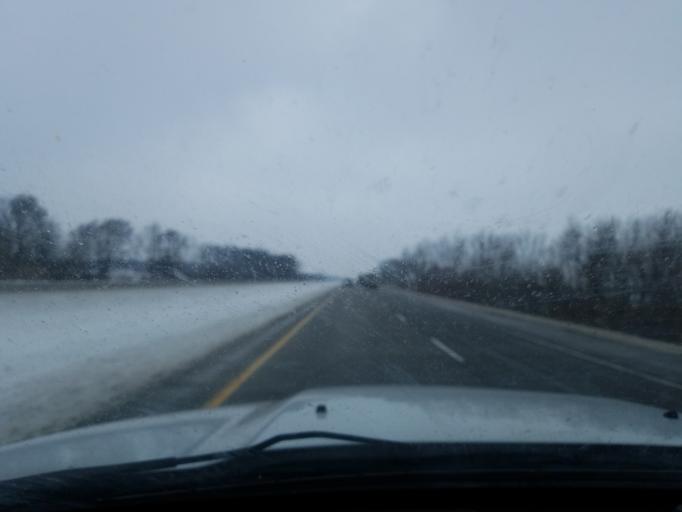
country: US
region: Indiana
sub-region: Marshall County
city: Argos
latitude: 41.1752
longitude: -86.2432
